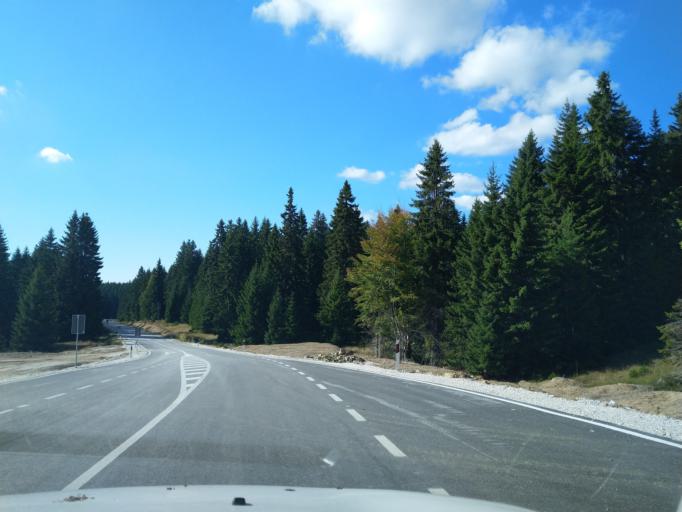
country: RS
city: Sokolovica
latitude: 43.2817
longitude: 20.3315
